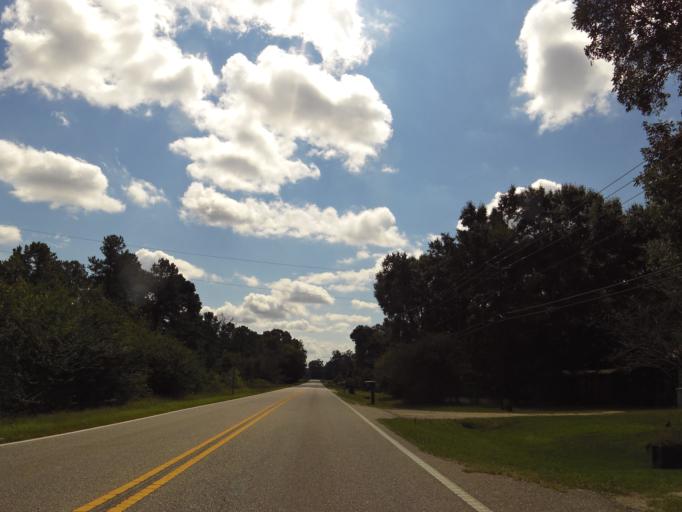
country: US
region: Alabama
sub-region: Dallas County
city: Selma
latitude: 32.4129
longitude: -87.0832
